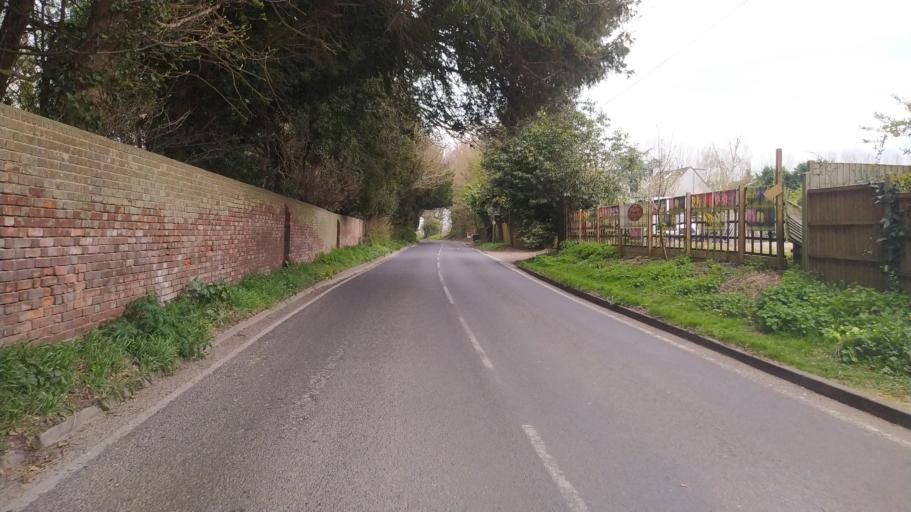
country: GB
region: England
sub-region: West Sussex
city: Boxgrove
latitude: 50.8395
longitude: -0.7407
